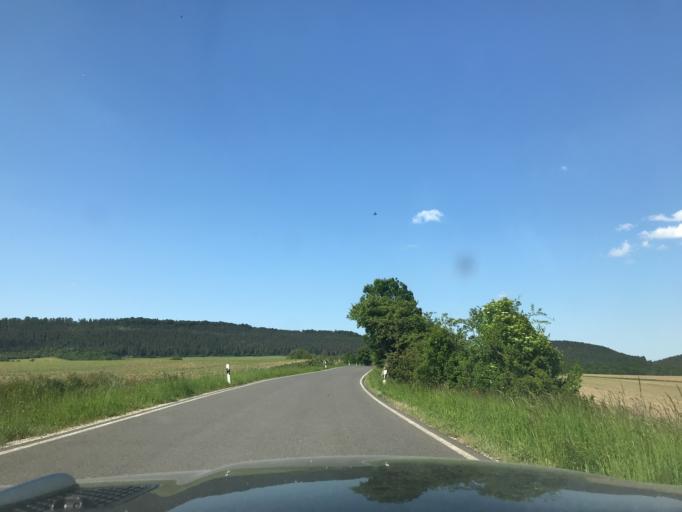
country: DE
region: Thuringia
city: Plaue
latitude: 50.7686
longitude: 10.9498
